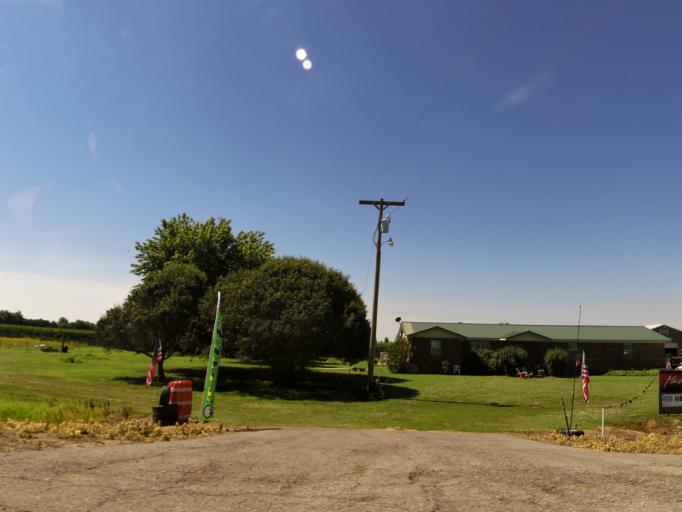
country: US
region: Missouri
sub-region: Dunklin County
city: Malden
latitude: 36.5528
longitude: -89.8849
